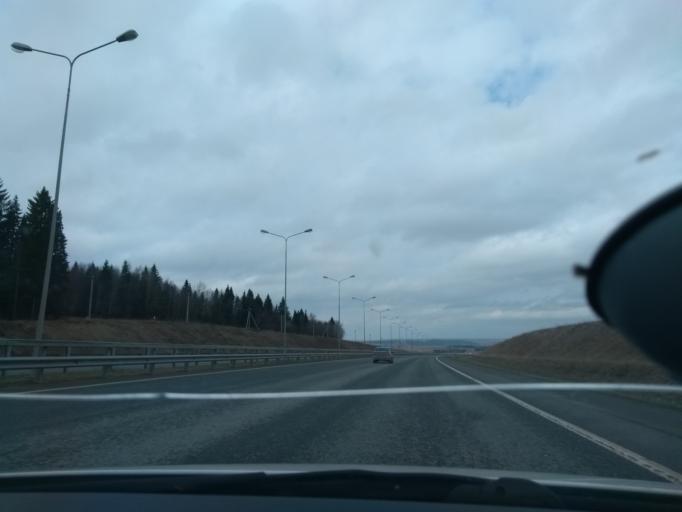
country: RU
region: Perm
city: Zvezdnyy
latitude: 57.7627
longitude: 56.3334
